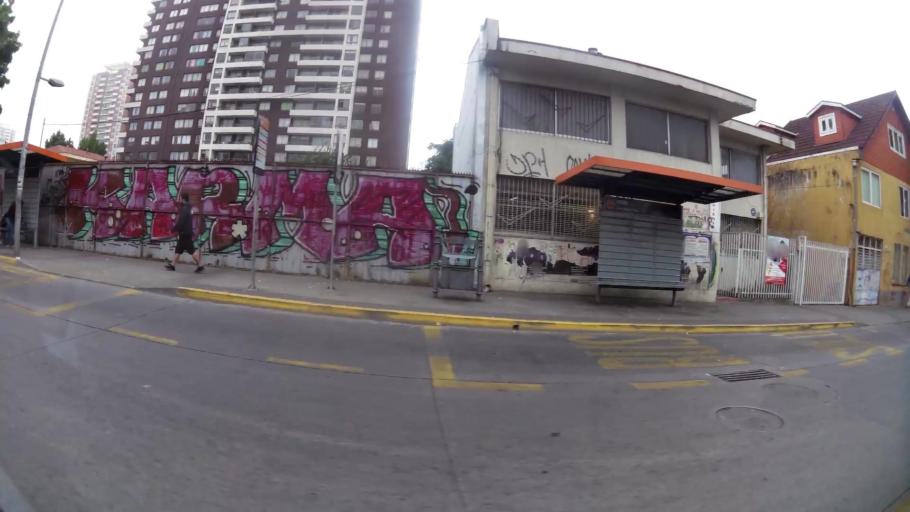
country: CL
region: Biobio
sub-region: Provincia de Concepcion
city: Concepcion
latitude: -36.8217
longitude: -73.0430
